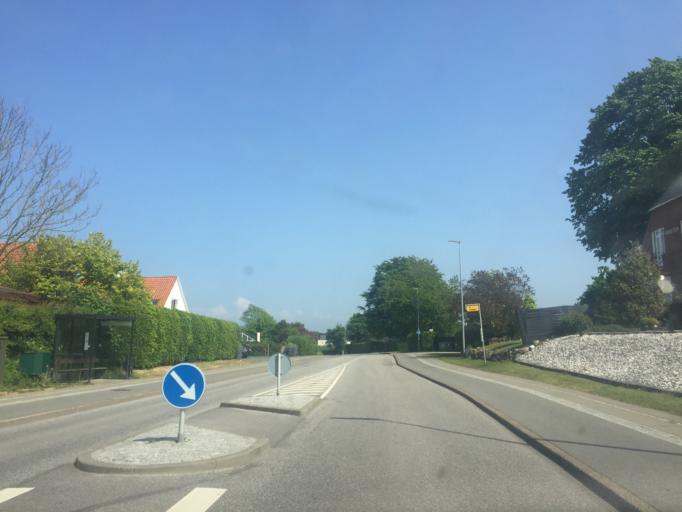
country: DK
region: South Denmark
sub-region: Kolding Kommune
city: Kolding
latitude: 55.4777
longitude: 9.5019
